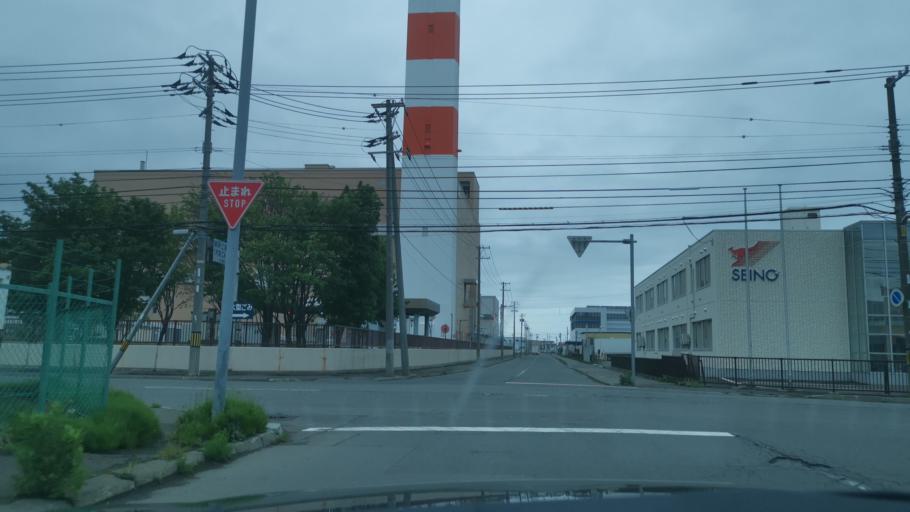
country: JP
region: Hokkaido
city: Sapporo
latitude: 43.1089
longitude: 141.2843
